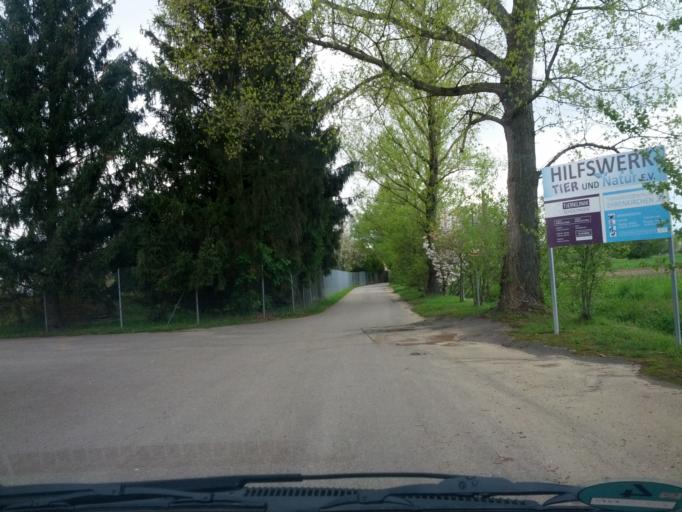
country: DE
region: Baden-Wuerttemberg
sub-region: Freiburg Region
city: Pfaffenweiler
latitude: 47.9505
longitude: 7.7380
